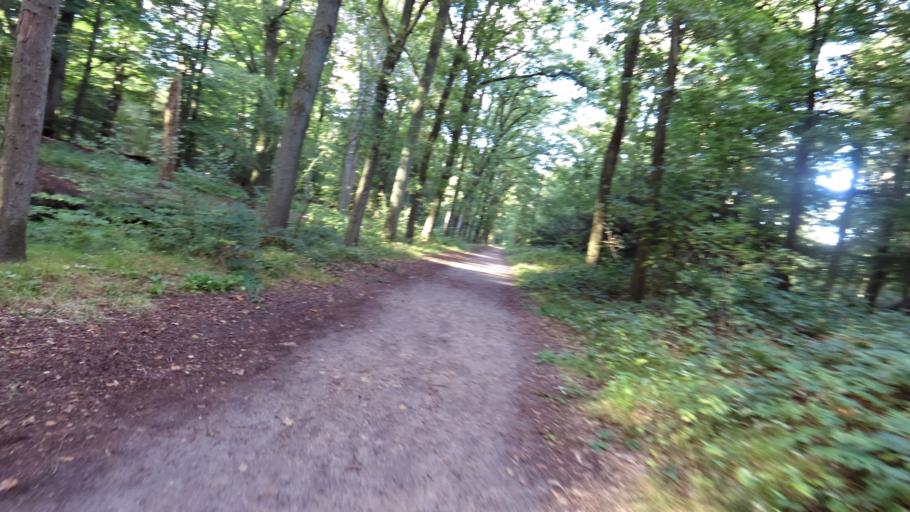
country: NL
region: Utrecht
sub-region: Gemeente De Bilt
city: De Bilt
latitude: 52.1072
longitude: 5.1961
